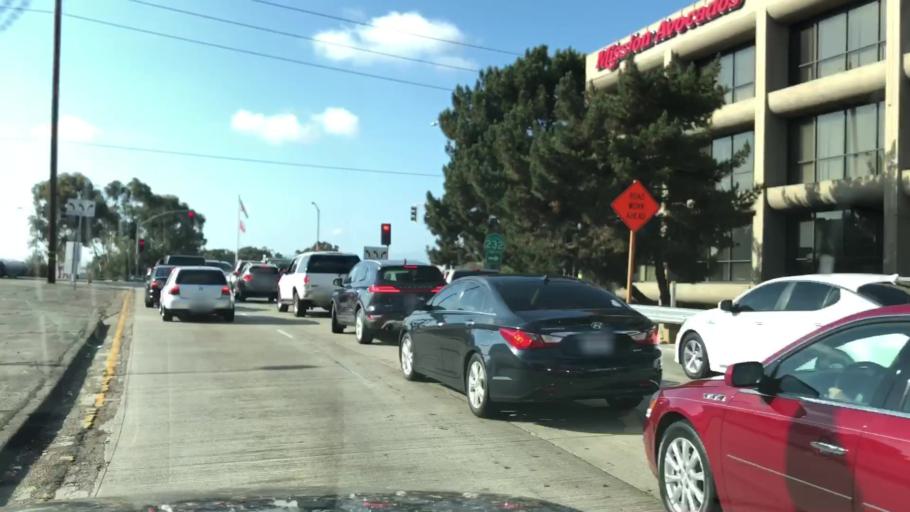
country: US
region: California
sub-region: Ventura County
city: El Rio
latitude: 34.2324
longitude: -119.1720
